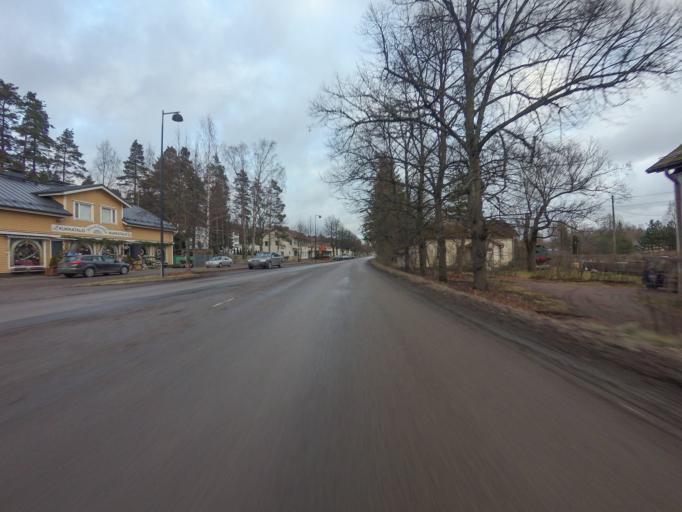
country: FI
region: Uusimaa
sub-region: Helsinki
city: Lohja
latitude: 60.2658
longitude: 24.1161
